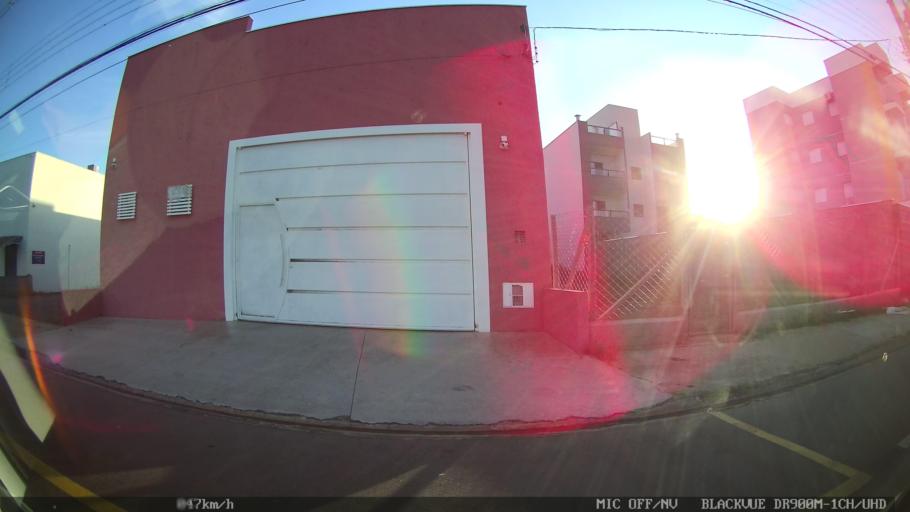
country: BR
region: Sao Paulo
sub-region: Franca
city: Franca
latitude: -20.5178
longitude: -47.3953
